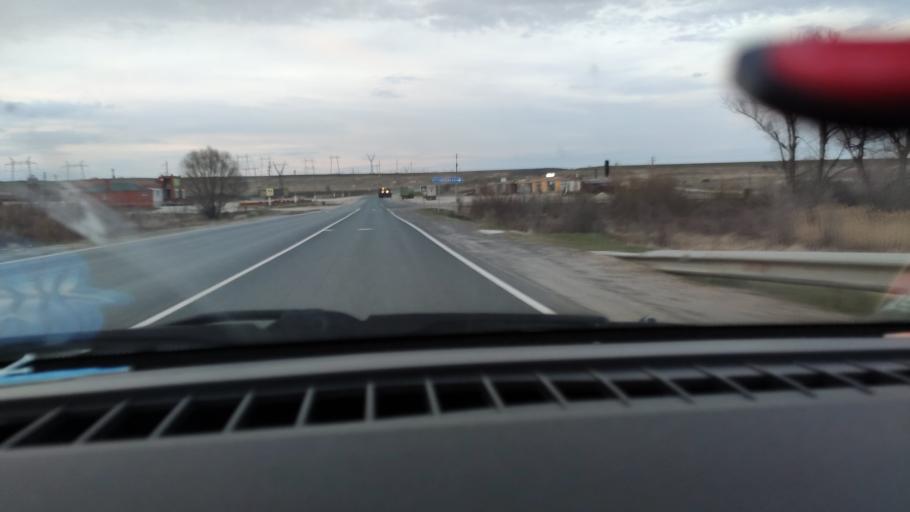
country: RU
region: Saratov
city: Sinodskoye
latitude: 51.9252
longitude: 46.5645
